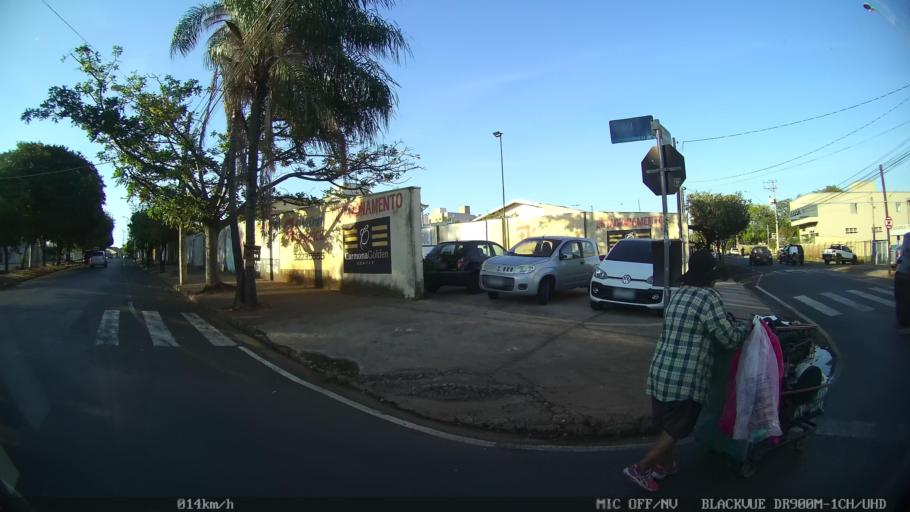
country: BR
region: Sao Paulo
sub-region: Sao Jose Do Rio Preto
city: Sao Jose do Rio Preto
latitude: -20.7951
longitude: -49.3575
